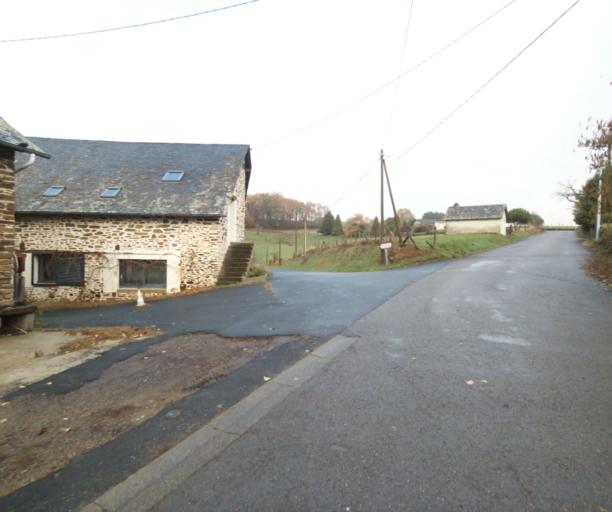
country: FR
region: Limousin
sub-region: Departement de la Correze
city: Cornil
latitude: 45.1927
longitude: 1.6432
